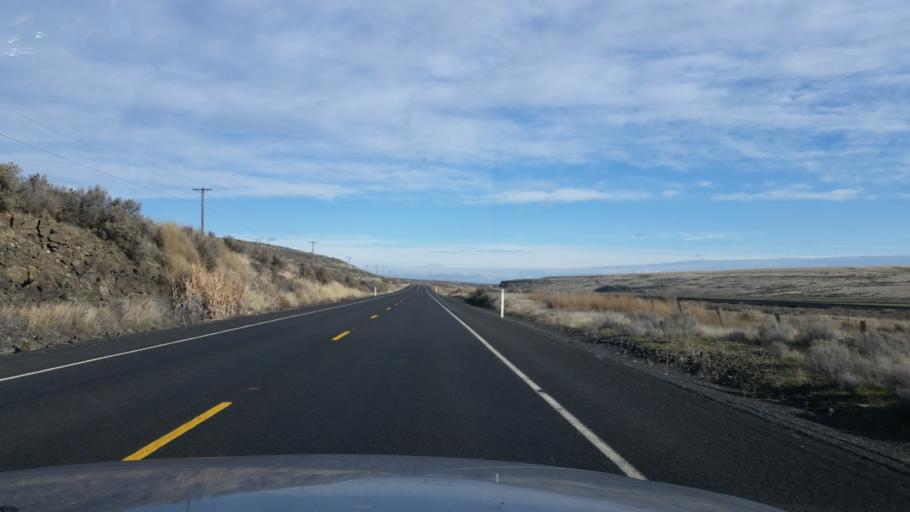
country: US
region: Washington
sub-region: Adams County
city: Ritzville
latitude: 47.3506
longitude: -118.5442
